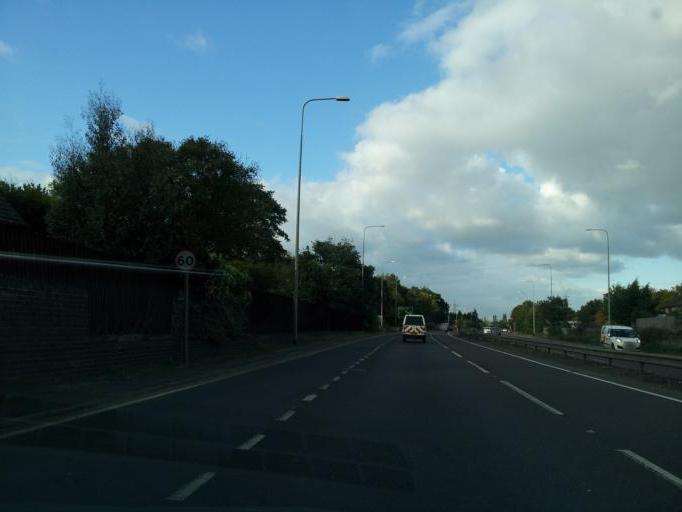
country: GB
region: England
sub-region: Cambridgeshire
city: Eaton Socon
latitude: 52.1952
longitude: -0.2985
